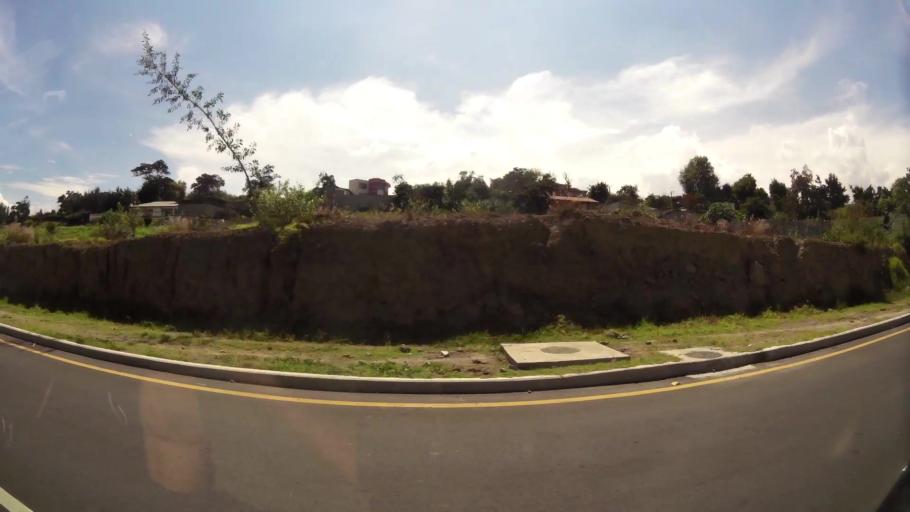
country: EC
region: Pichincha
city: Sangolqui
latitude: -0.2168
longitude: -78.3904
